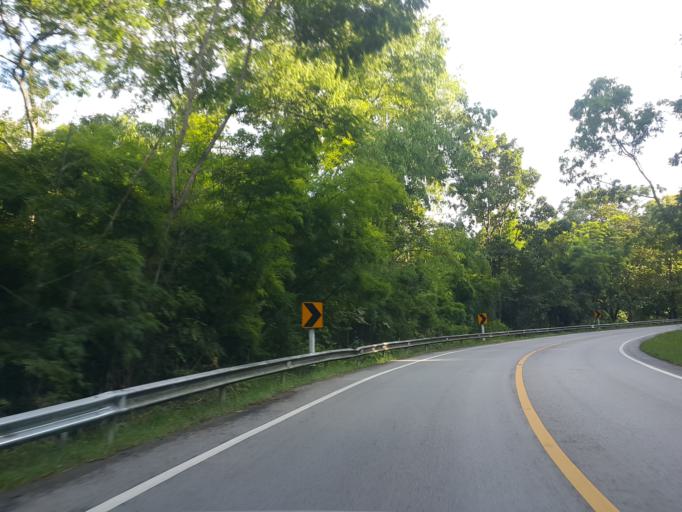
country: TH
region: Chiang Mai
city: Mae Taeng
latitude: 19.0952
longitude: 99.1439
